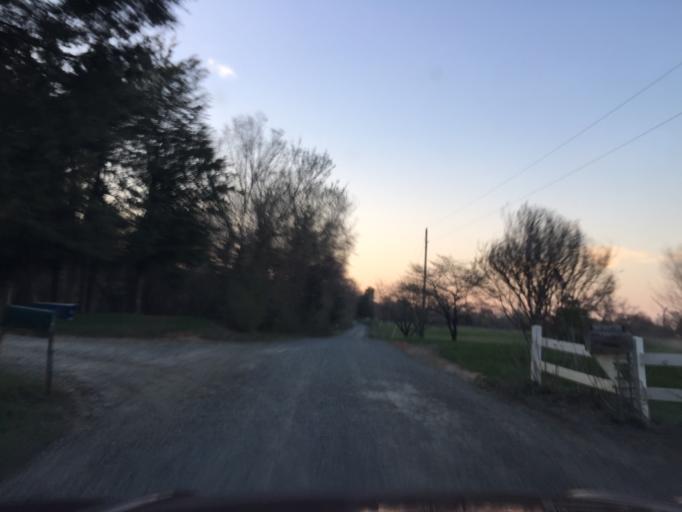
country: US
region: Virginia
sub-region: Loudoun County
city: Lovettsville
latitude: 39.2837
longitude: -77.5945
